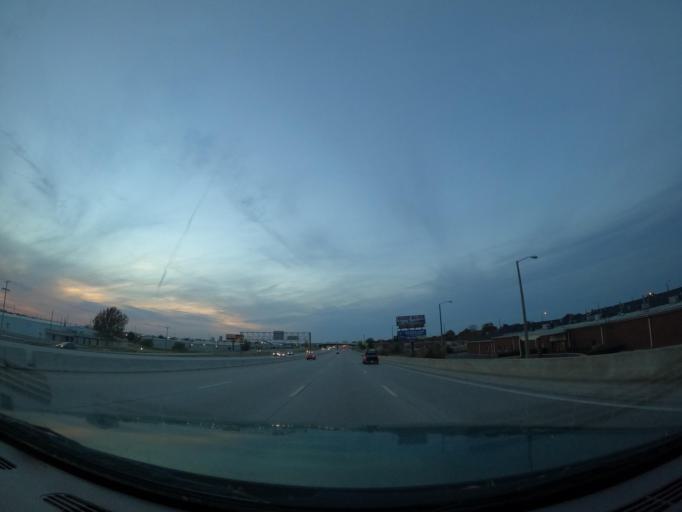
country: US
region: Oklahoma
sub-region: Tulsa County
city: Broken Arrow
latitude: 36.1026
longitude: -95.8716
